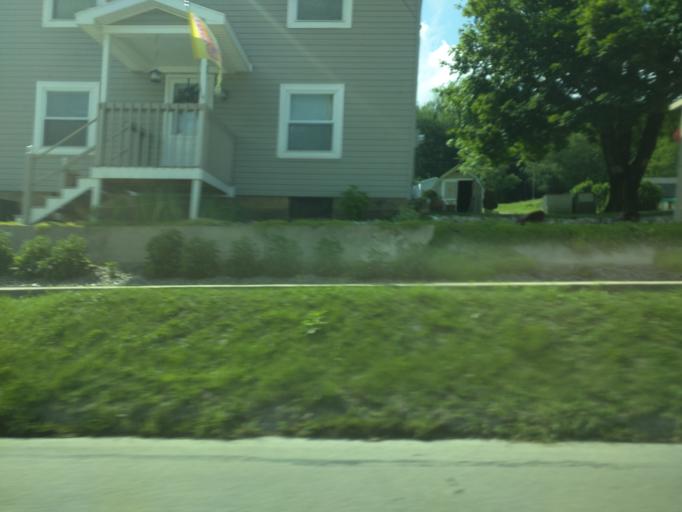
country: US
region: Pennsylvania
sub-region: Indiana County
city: Chevy Chase Heights
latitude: 40.7949
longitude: -79.1778
